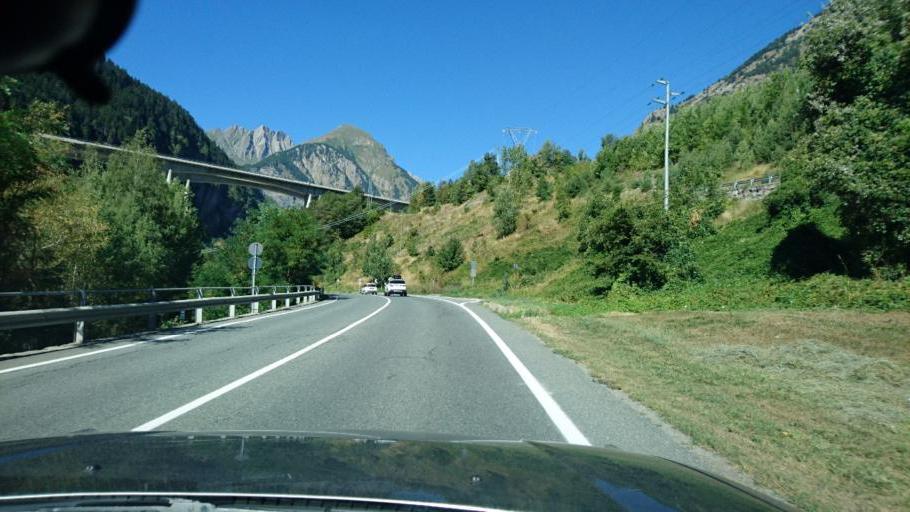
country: IT
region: Aosta Valley
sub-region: Valle d'Aosta
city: Morgex
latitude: 45.7606
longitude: 7.0216
